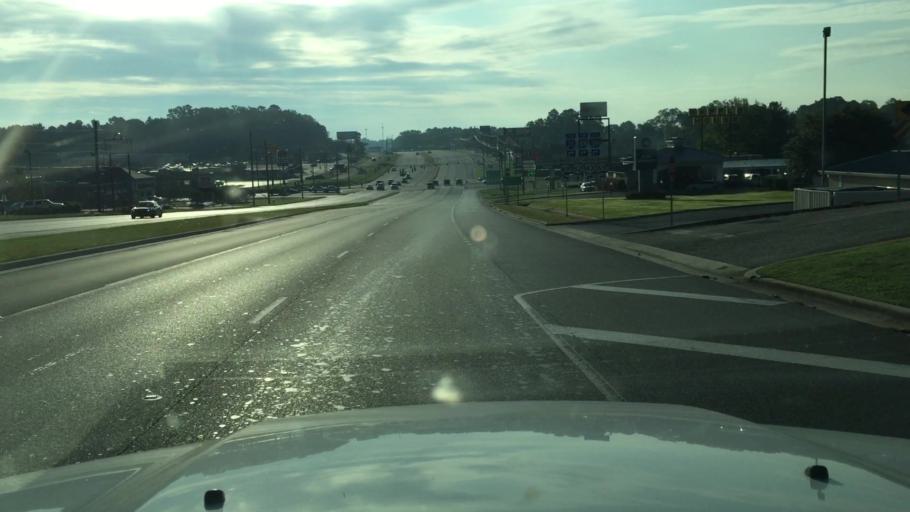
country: US
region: Alabama
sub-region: Tuscaloosa County
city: Northport
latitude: 33.2398
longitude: -87.5795
